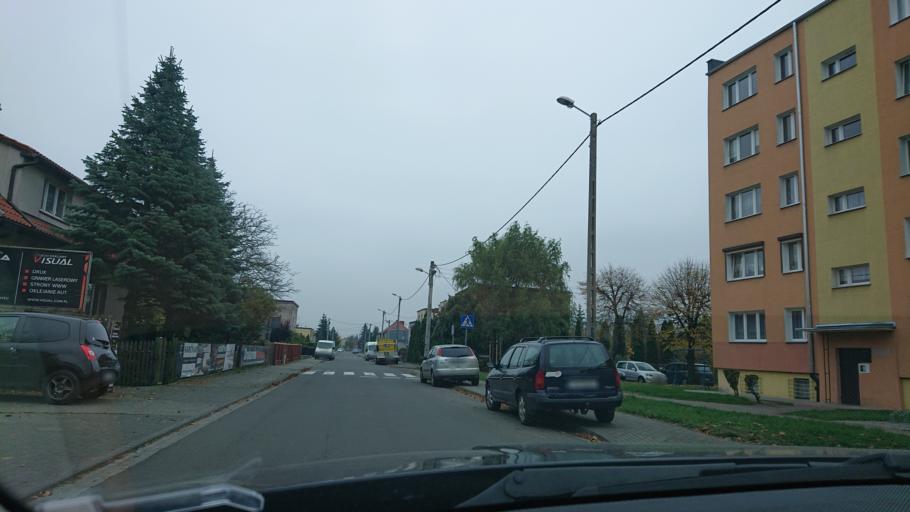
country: PL
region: Greater Poland Voivodeship
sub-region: Powiat gnieznienski
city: Gniezno
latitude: 52.5402
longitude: 17.6235
